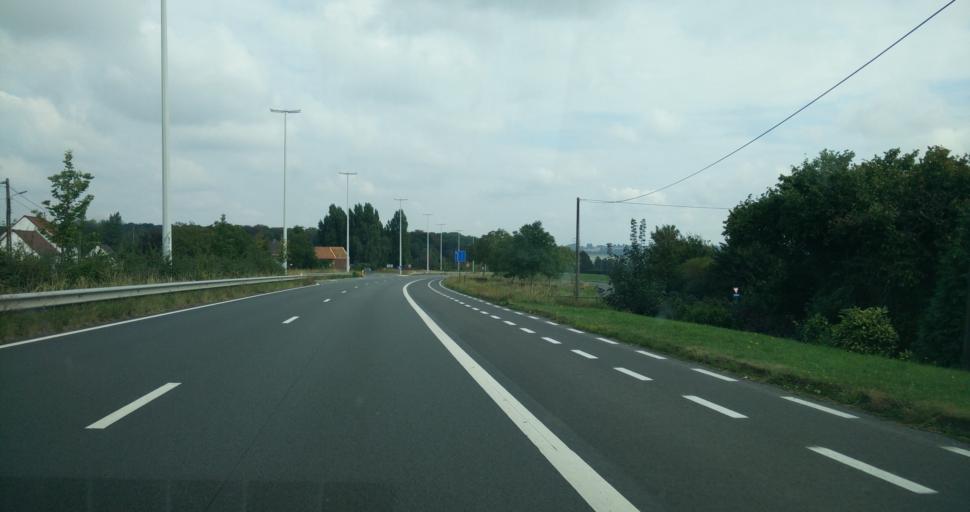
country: BE
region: Flanders
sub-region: Provincie Oost-Vlaanderen
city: Ronse
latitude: 50.7995
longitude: 3.5921
